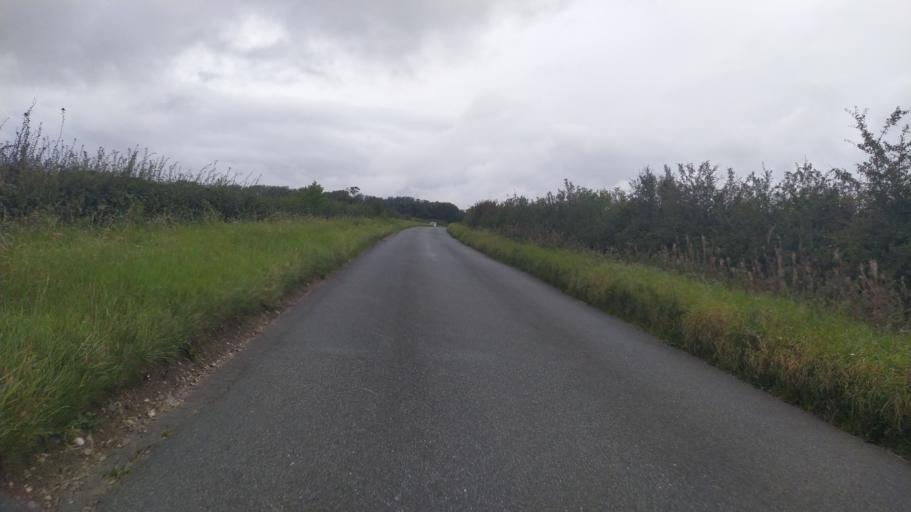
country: GB
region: England
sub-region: Dorset
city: Dorchester
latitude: 50.7993
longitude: -2.4455
